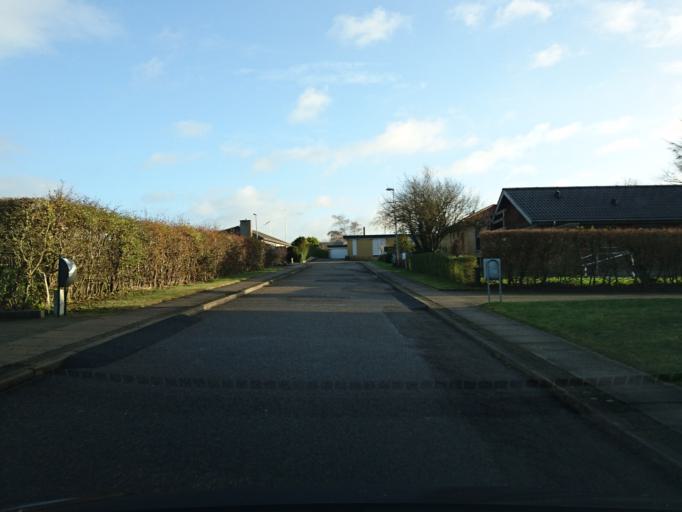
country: DK
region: North Denmark
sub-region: Alborg Kommune
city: Aalborg
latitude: 57.0153
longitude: 9.9351
